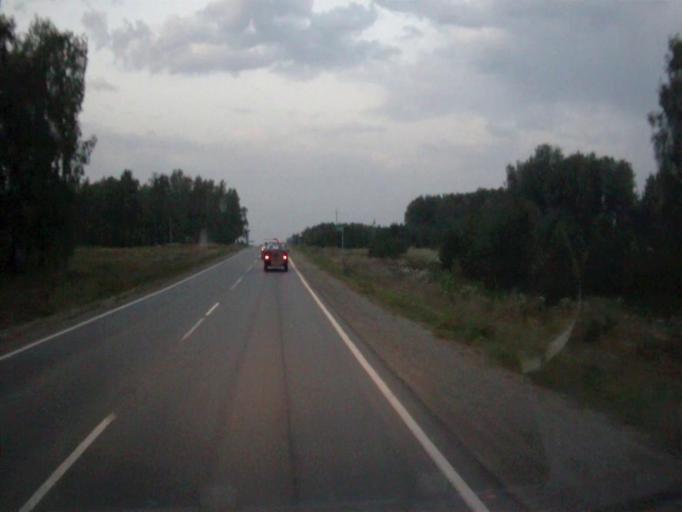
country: RU
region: Chelyabinsk
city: Timiryazevskiy
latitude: 55.2049
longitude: 60.7765
